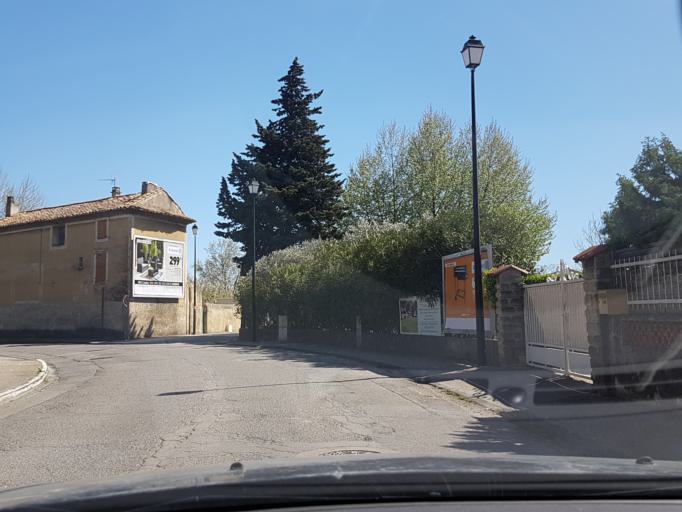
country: FR
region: Provence-Alpes-Cote d'Azur
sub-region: Departement du Vaucluse
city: Sarrians
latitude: 44.0805
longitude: 4.9713
